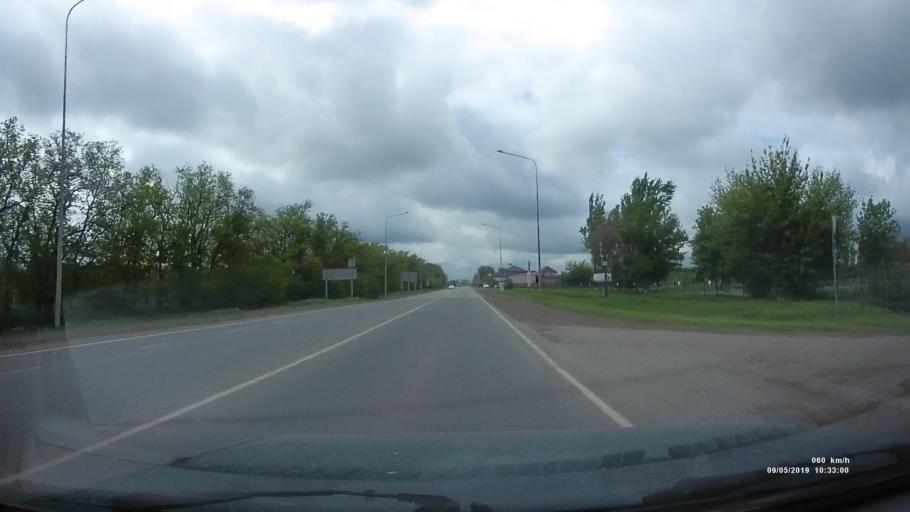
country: RU
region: Rostov
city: Azov
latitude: 47.0673
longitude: 39.4254
